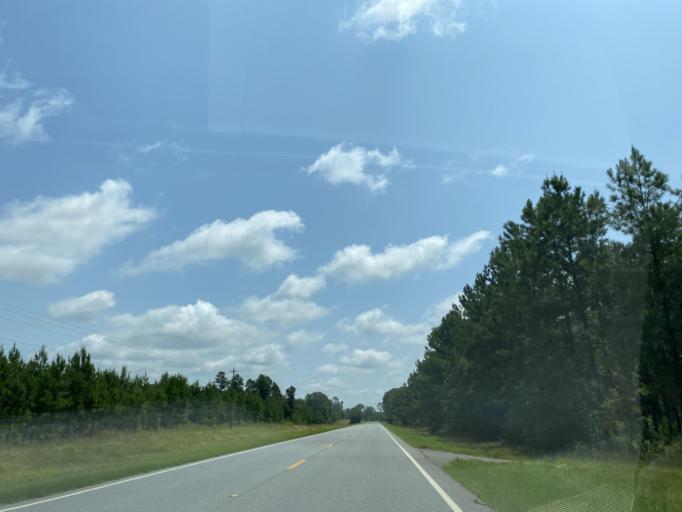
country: US
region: Georgia
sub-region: Telfair County
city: Helena
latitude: 32.0296
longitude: -83.0165
